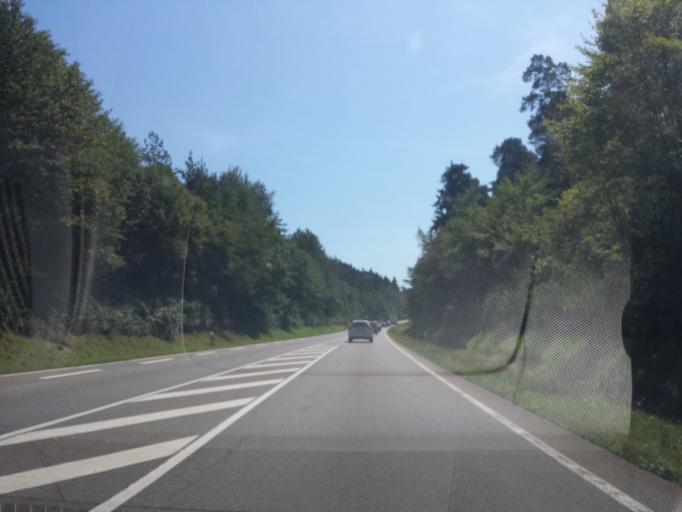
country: DE
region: Bavaria
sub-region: Lower Bavaria
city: Stallwang
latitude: 49.0601
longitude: 12.6432
